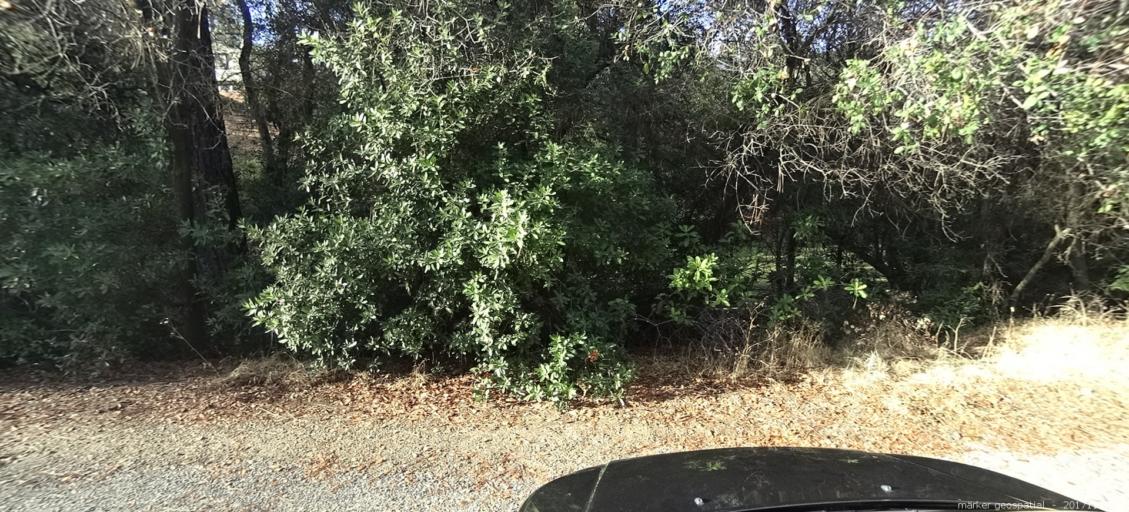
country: US
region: California
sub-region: Shasta County
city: Shasta
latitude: 40.5814
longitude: -122.4699
